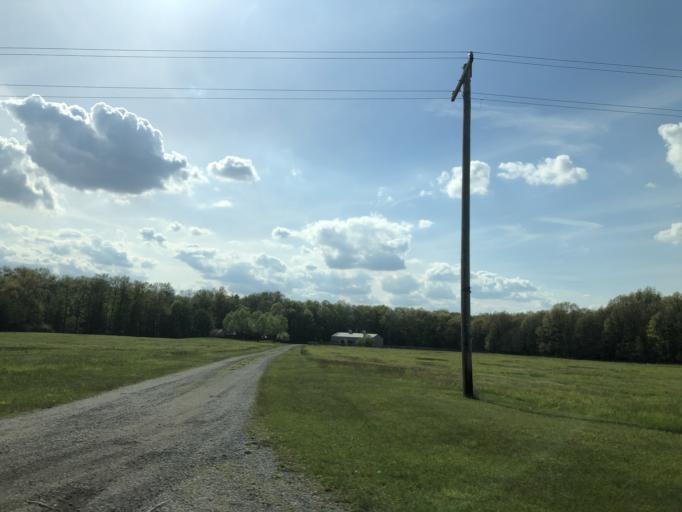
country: US
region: Michigan
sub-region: Hillsdale County
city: Reading
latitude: 41.7475
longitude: -84.8152
